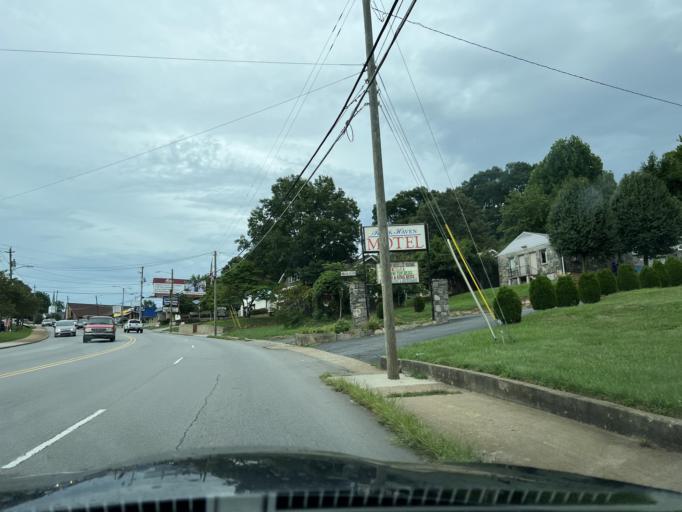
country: US
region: North Carolina
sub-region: Buncombe County
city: Asheville
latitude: 35.5781
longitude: -82.6094
